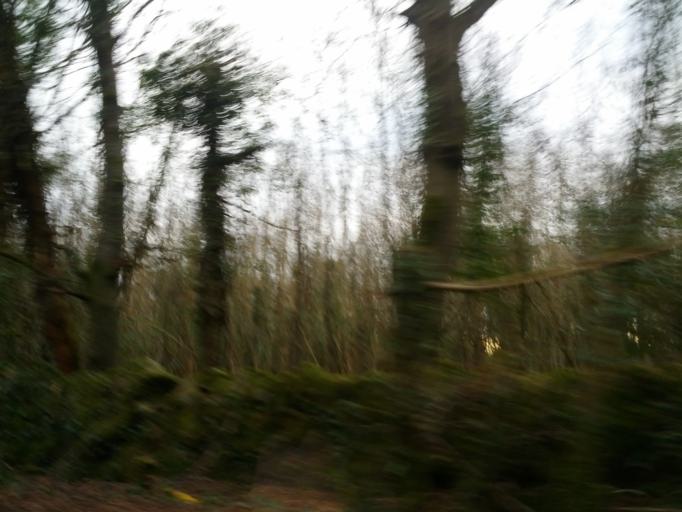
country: IE
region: Connaught
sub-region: County Galway
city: Oranmore
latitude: 53.1773
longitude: -8.8970
